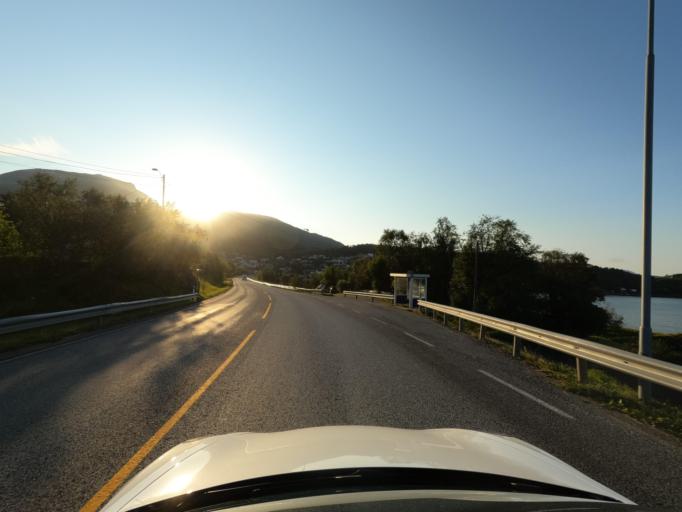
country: NO
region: Troms
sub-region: Harstad
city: Harstad
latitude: 68.7441
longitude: 16.5660
